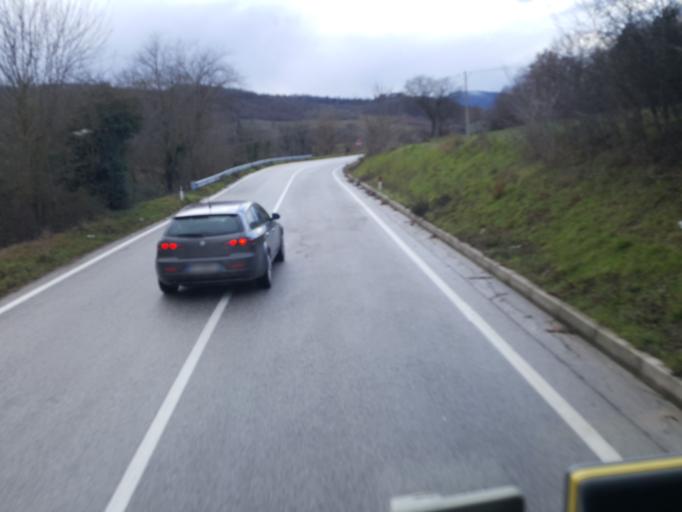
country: IT
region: The Marches
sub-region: Provincia di Macerata
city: Camerino
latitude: 43.1106
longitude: 13.1194
